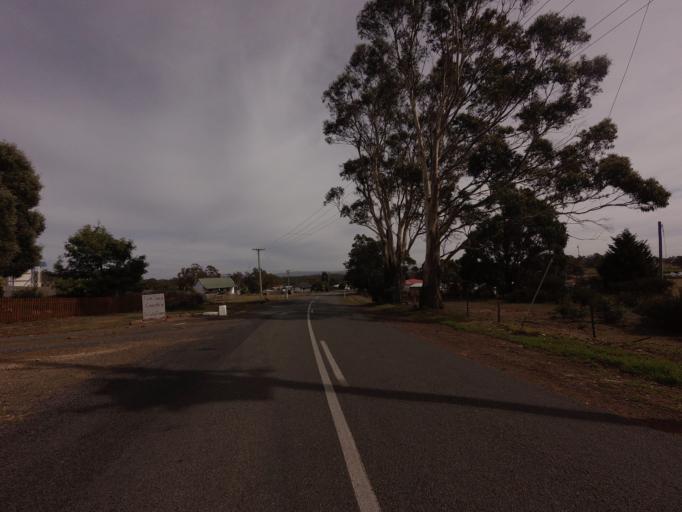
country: AU
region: Tasmania
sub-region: Brighton
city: Bridgewater
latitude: -42.3586
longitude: 147.4082
